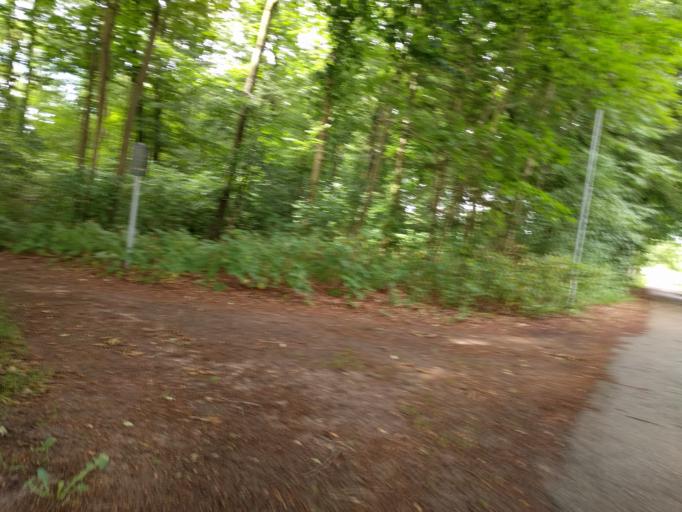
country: DK
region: Central Jutland
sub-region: Skanderborg Kommune
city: Ry
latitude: 56.0807
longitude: 9.7647
